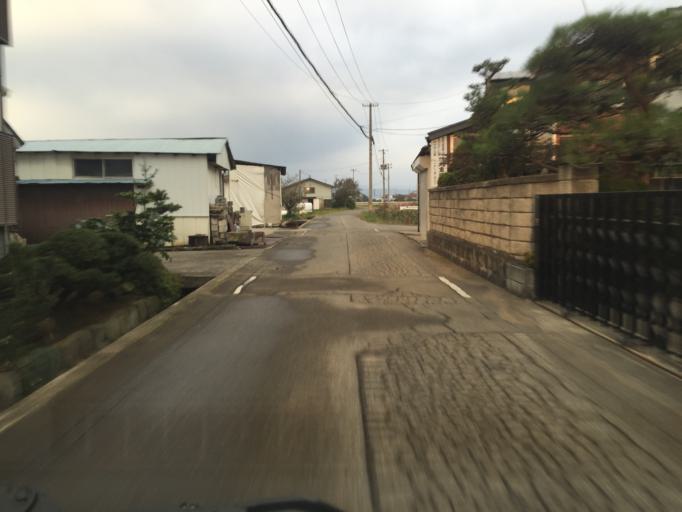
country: JP
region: Fukushima
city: Kitakata
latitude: 37.5355
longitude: 139.9085
